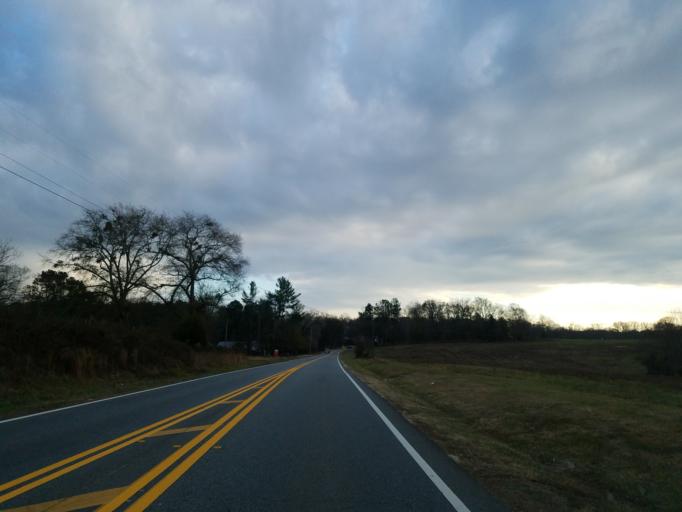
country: US
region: Georgia
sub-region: Forsyth County
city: Cumming
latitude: 34.2908
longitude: -84.0881
